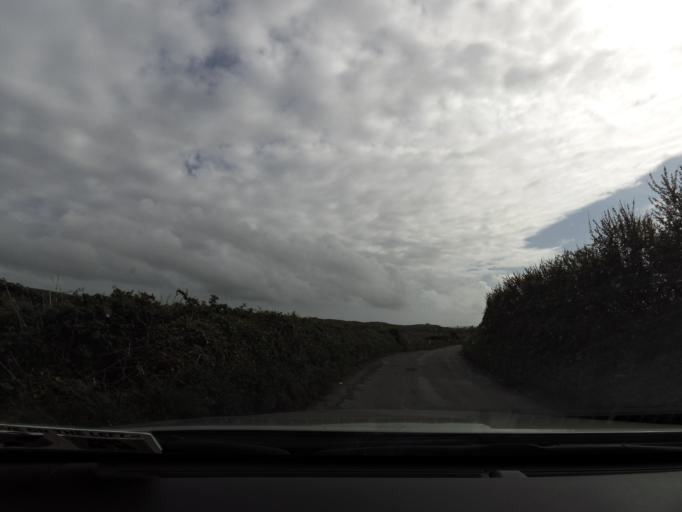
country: IE
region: Connaught
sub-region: County Galway
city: Bearna
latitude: 53.0457
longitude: -9.3414
